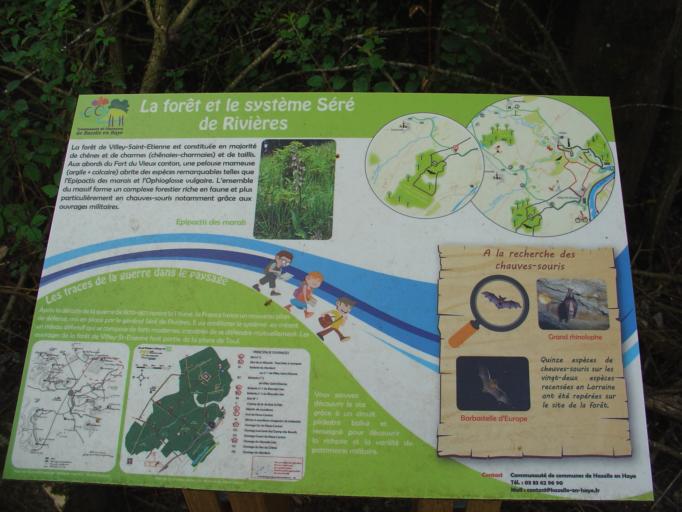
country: FR
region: Lorraine
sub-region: Departement de Meurthe-et-Moselle
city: Villey-Saint-Etienne
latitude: 48.7269
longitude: 5.9592
